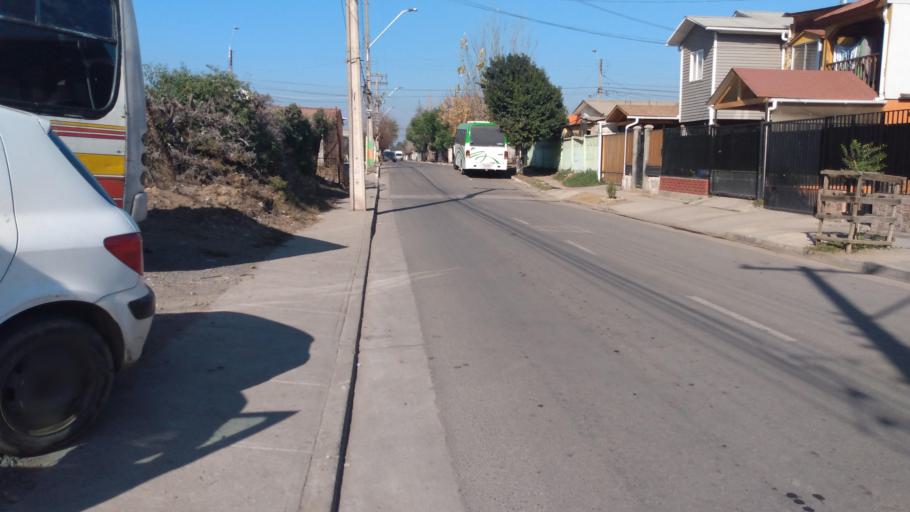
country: CL
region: Valparaiso
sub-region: Provincia de Quillota
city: Hacienda La Calera
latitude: -32.7293
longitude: -71.2060
